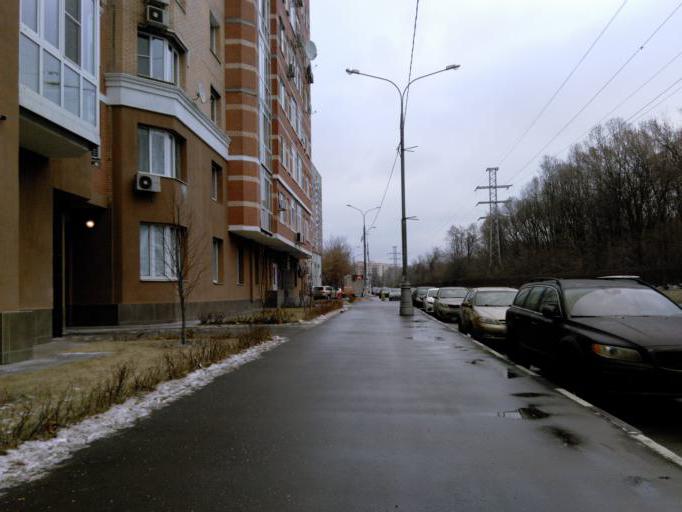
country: RU
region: Moskovskaya
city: Semenovskoye
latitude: 55.6683
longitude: 37.5338
